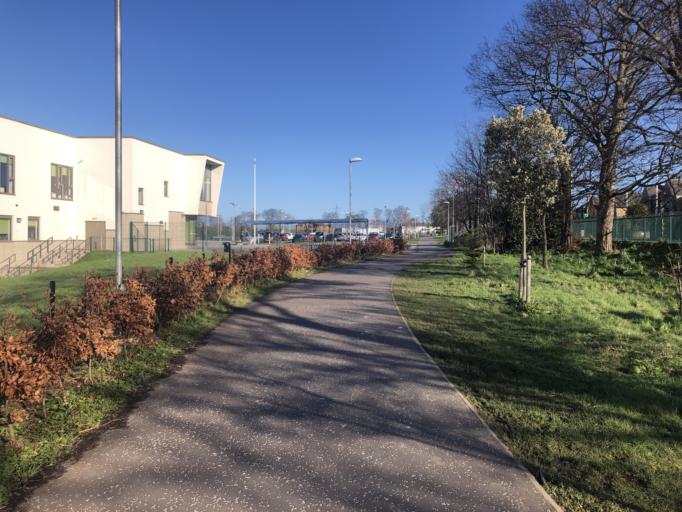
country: GB
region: Scotland
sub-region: West Lothian
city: Seafield
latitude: 55.9440
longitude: -3.1138
